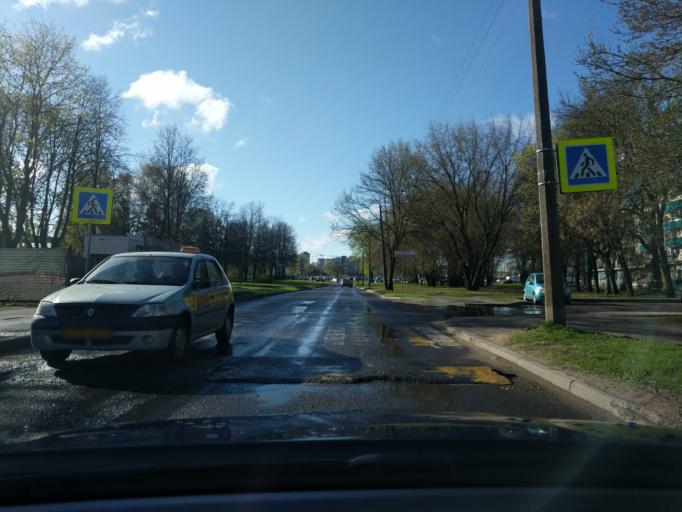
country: BY
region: Minsk
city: Novoye Medvezhino
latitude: 53.9000
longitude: 27.5063
